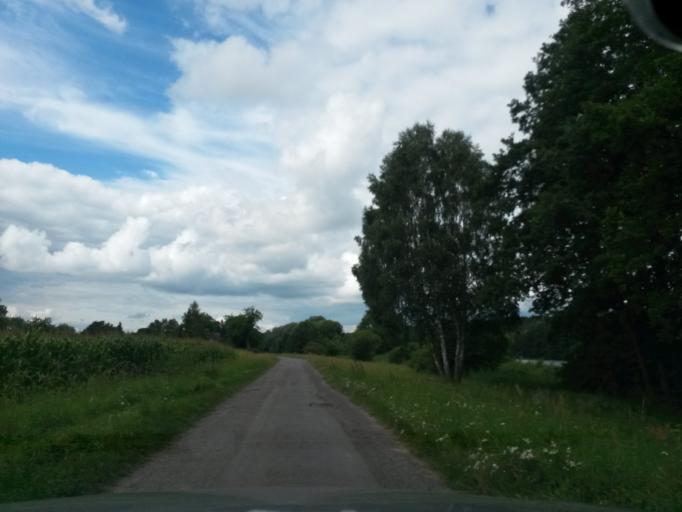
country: DE
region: Brandenburg
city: Oderberg
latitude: 52.8690
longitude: 14.1067
